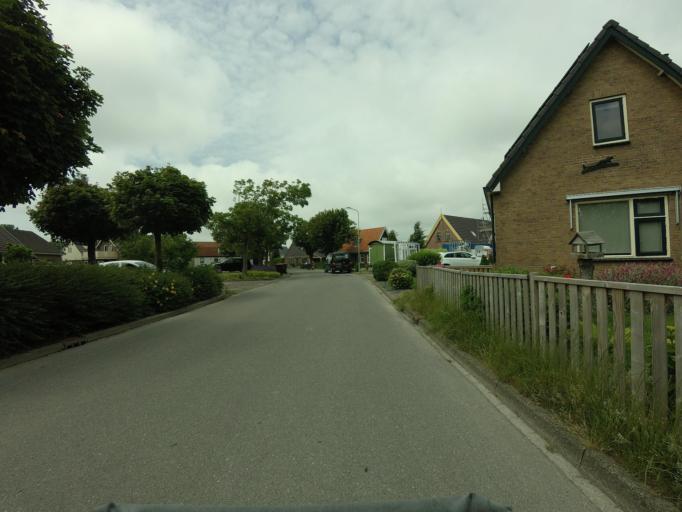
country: NL
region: North Holland
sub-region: Gemeente Schagen
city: Harenkarspel
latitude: 52.7399
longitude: 4.7588
